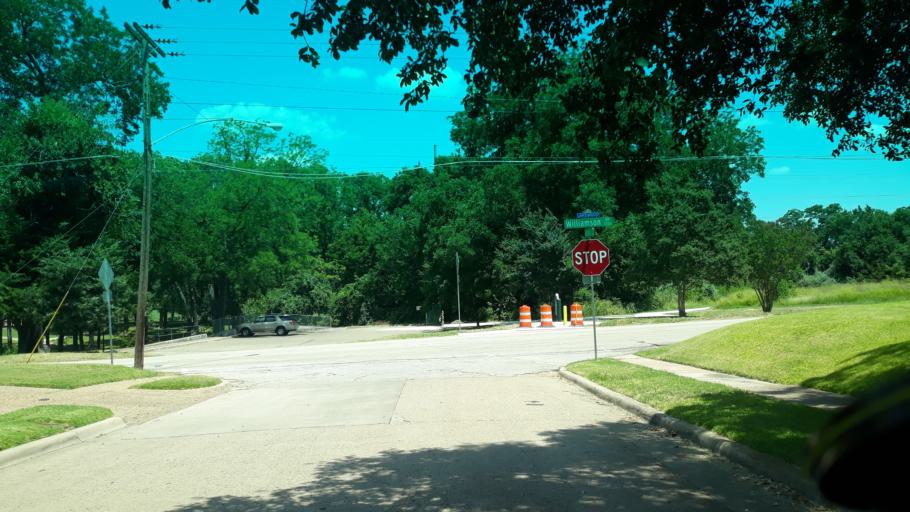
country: US
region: Texas
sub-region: Dallas County
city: Highland Park
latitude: 32.8304
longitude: -96.7356
